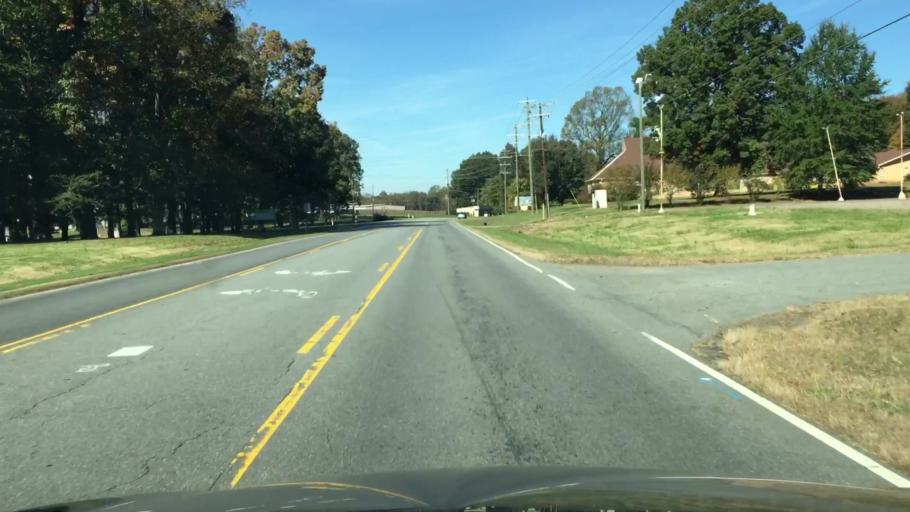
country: US
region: North Carolina
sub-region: Rockingham County
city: Reidsville
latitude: 36.3307
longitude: -79.6490
